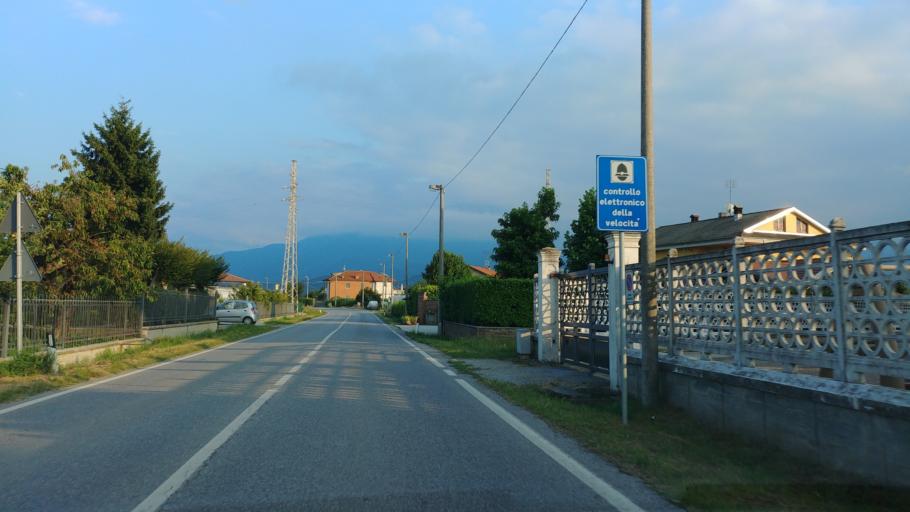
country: IT
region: Piedmont
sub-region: Provincia di Cuneo
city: Cuneo
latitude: 44.3704
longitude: 7.5788
